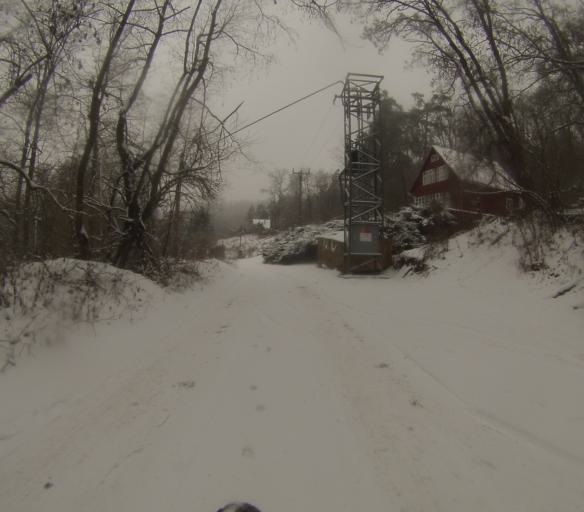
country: CZ
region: South Moravian
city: Orechov
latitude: 49.1350
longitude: 16.5311
